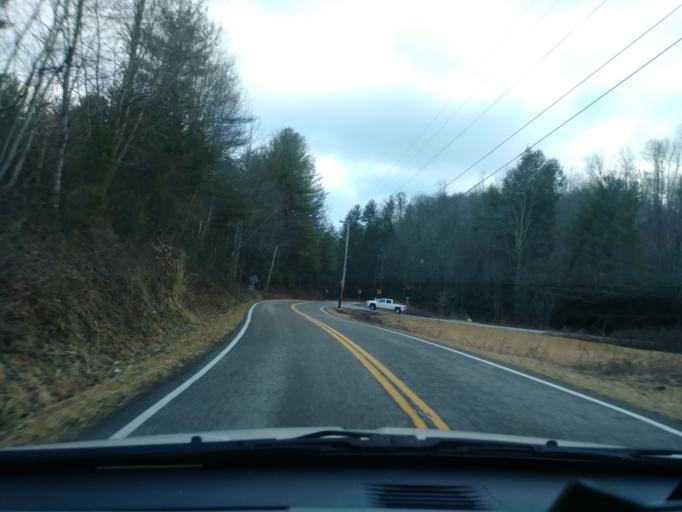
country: US
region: Tennessee
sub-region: Unicoi County
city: Unicoi
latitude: 36.2057
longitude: -82.2338
